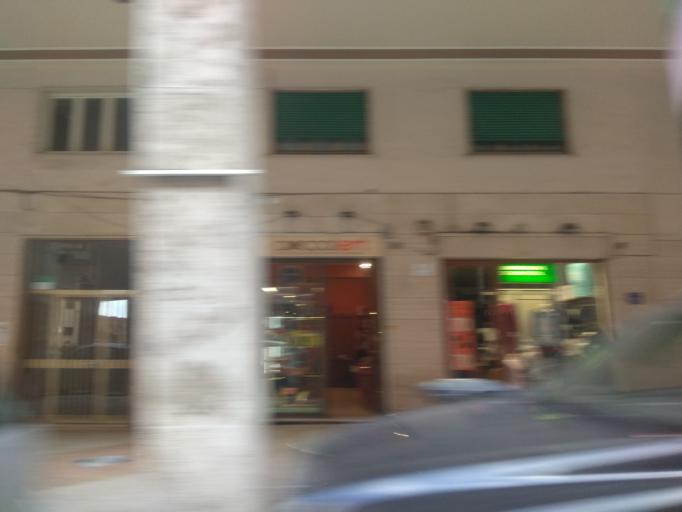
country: IT
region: Latium
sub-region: Citta metropolitana di Roma Capitale
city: Civitavecchia
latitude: 42.0937
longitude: 11.7908
